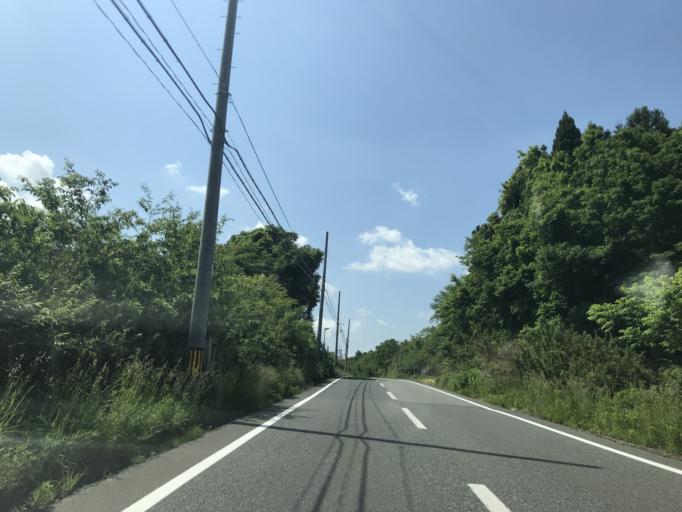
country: JP
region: Miyagi
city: Furukawa
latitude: 38.7215
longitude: 140.9484
